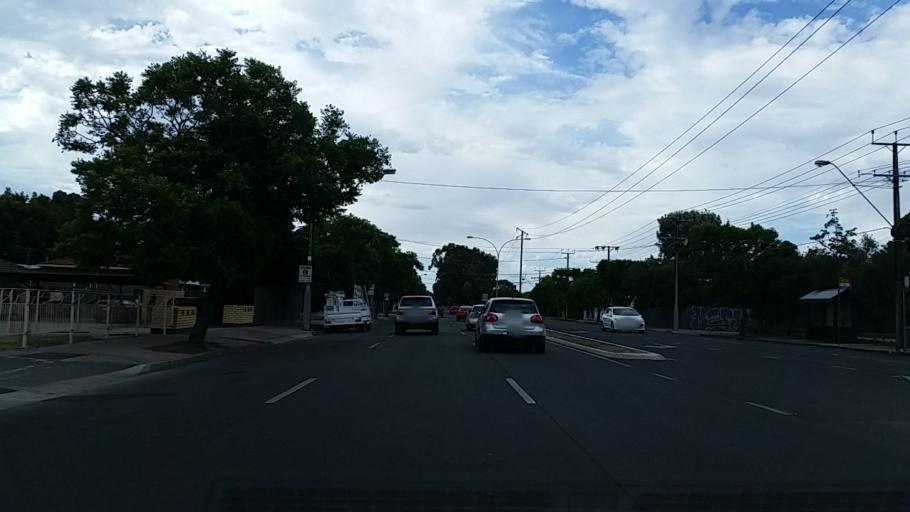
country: AU
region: South Australia
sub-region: Mitcham
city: Clapham
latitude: -34.9900
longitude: 138.5925
